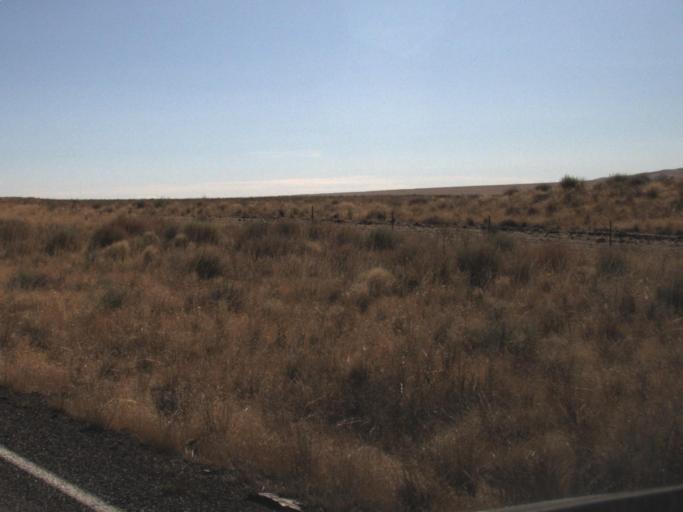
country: US
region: Washington
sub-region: Benton County
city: Benton City
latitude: 46.5066
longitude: -119.6323
